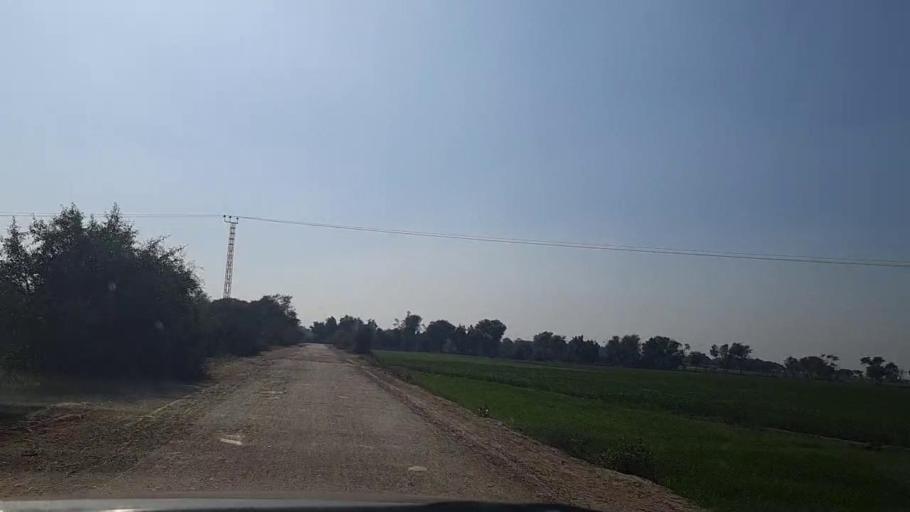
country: PK
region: Sindh
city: Sehwan
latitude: 26.2805
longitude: 68.0401
